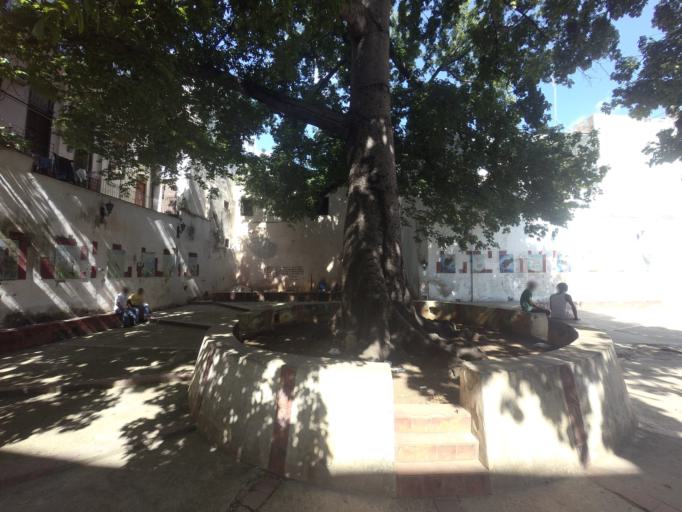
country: CU
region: La Habana
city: La Habana Vieja
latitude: 23.1300
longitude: -82.3511
